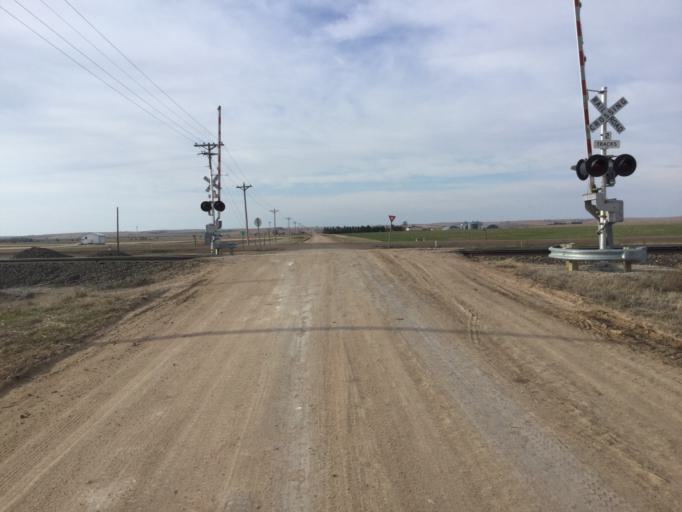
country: US
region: Kansas
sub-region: Ellis County
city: Ellis
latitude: 38.9510
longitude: -99.6507
